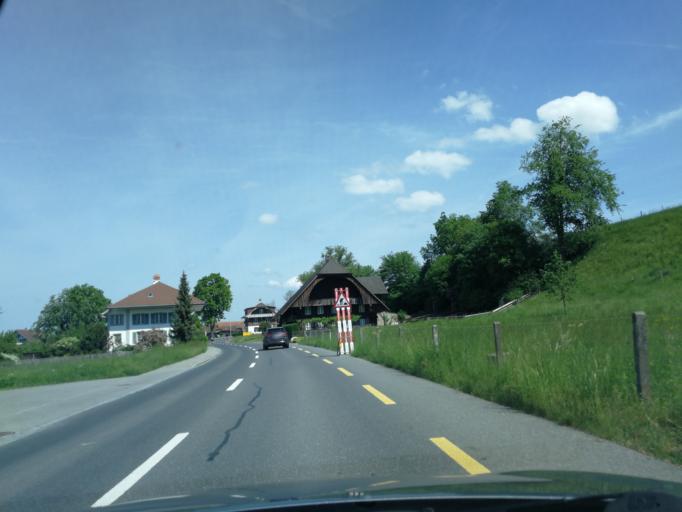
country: CH
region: Bern
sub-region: Bern-Mittelland District
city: Niederwichtrach
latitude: 46.8398
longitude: 7.5777
